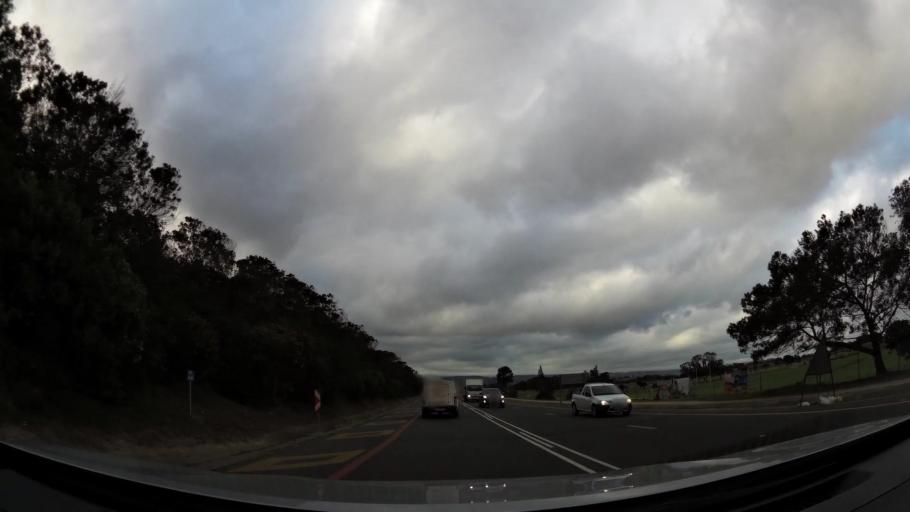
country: ZA
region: Western Cape
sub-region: Eden District Municipality
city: Plettenberg Bay
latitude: -34.0390
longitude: 23.3706
